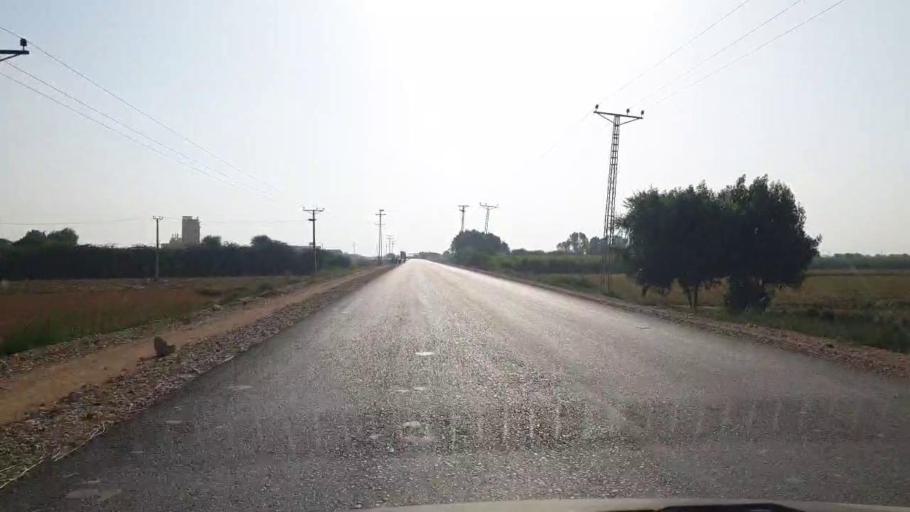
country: PK
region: Sindh
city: Badin
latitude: 24.6621
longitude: 68.8764
